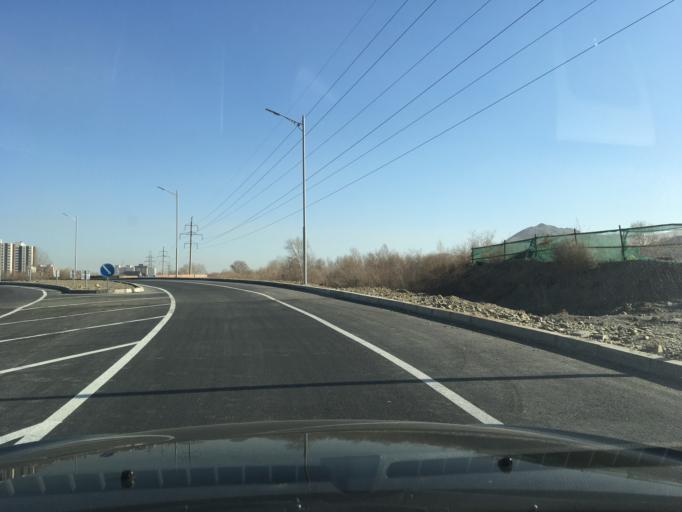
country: MN
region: Ulaanbaatar
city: Ulaanbaatar
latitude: 47.8891
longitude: 106.8656
